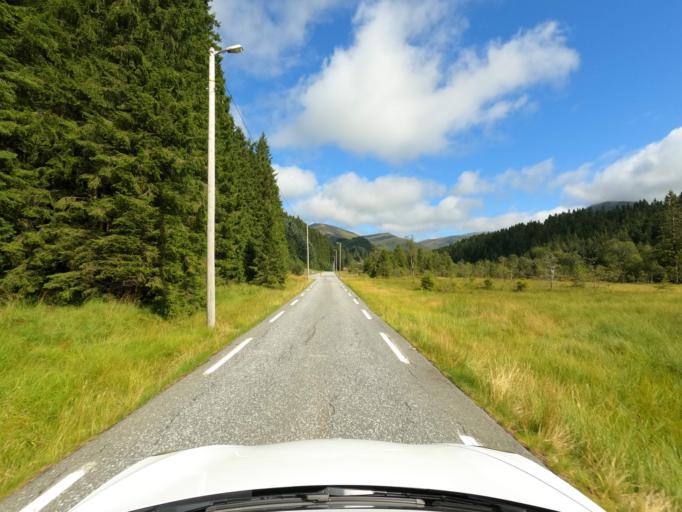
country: NO
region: Hordaland
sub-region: Bergen
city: Espeland
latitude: 60.3304
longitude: 5.4873
